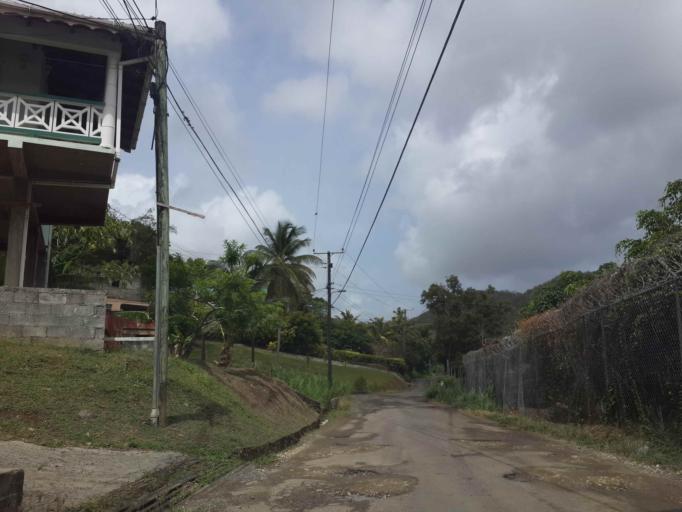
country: LC
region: Castries Quarter
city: Bisee
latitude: 14.0231
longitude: -60.9581
